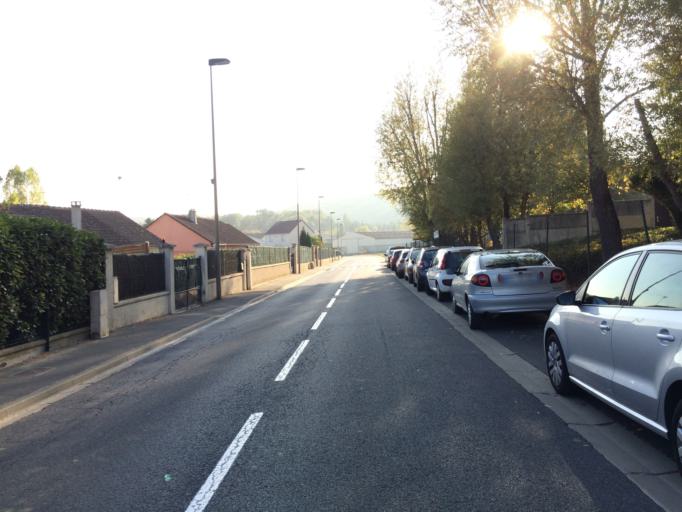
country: FR
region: Ile-de-France
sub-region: Departement de l'Essonne
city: Villebon-sur-Yvette
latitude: 48.6952
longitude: 2.2469
